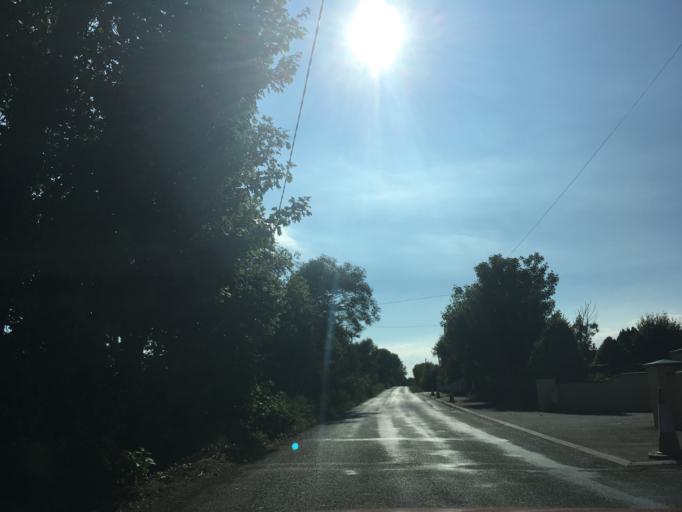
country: IE
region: Leinster
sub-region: Loch Garman
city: Rosslare
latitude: 52.2398
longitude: -6.4009
